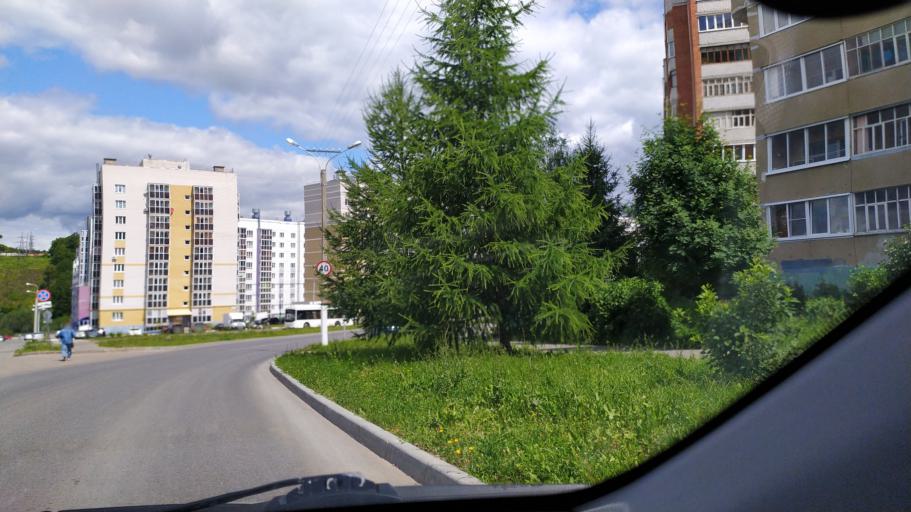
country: RU
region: Chuvashia
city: Novyye Lapsary
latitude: 56.1211
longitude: 47.1747
